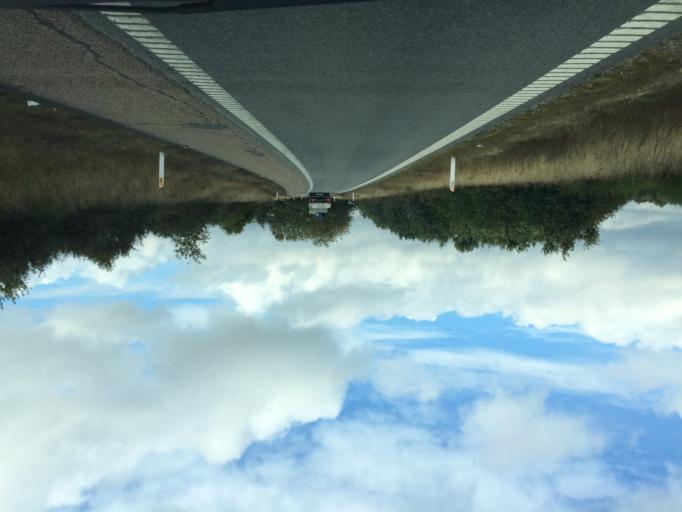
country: DK
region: North Denmark
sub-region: Bronderslev Kommune
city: Hjallerup
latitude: 57.1670
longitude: 10.1888
